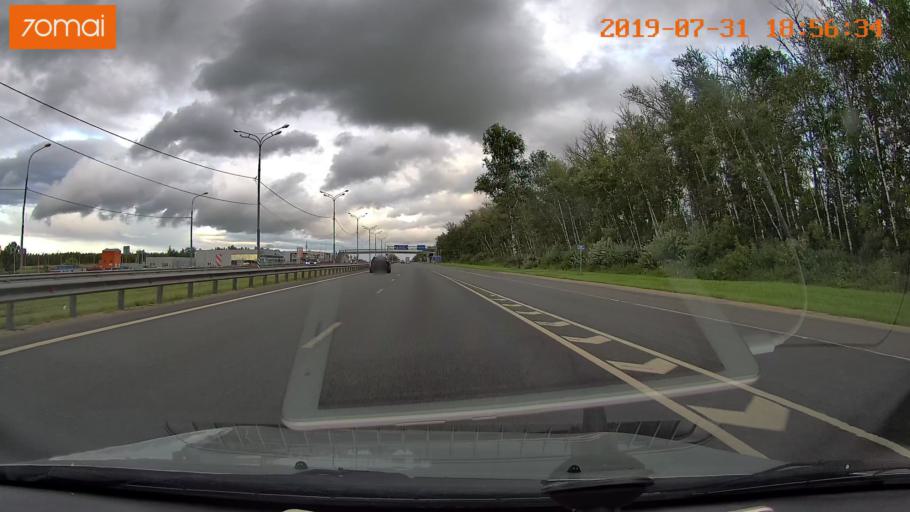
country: RU
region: Moskovskaya
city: Raduzhnyy
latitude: 55.1618
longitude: 38.6799
